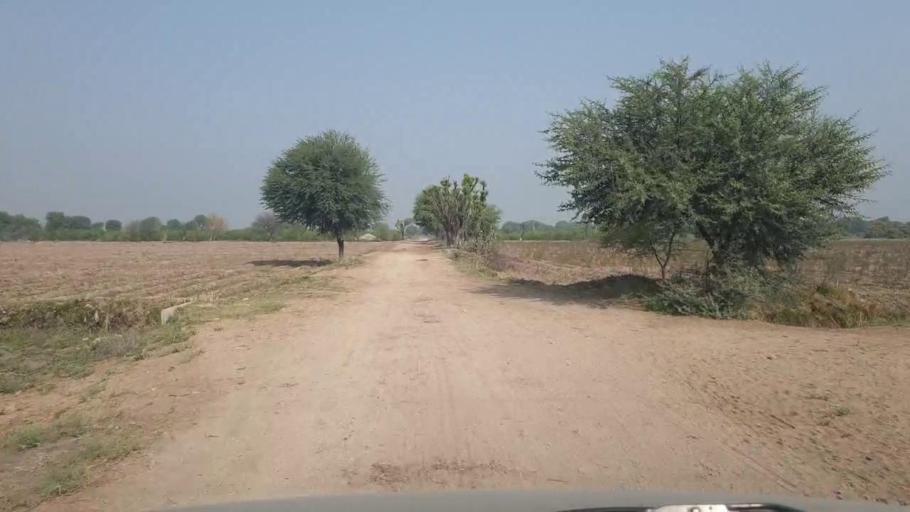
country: PK
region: Sindh
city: Umarkot
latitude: 25.3913
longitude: 69.7105
